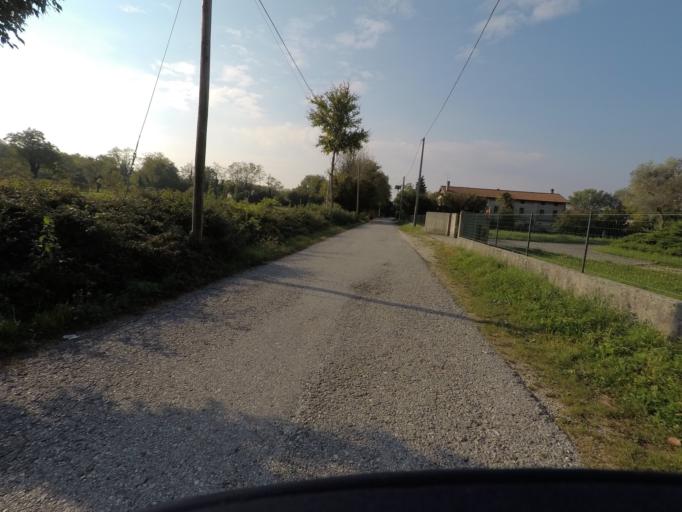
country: IT
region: Friuli Venezia Giulia
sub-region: Provincia di Udine
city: Gemona
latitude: 46.2589
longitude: 13.1374
